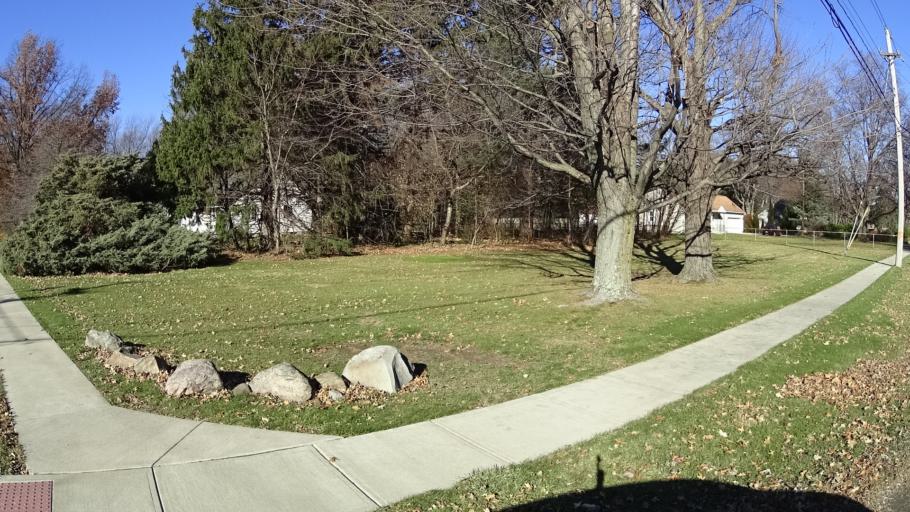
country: US
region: Ohio
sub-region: Lorain County
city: Avon
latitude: 41.4306
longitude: -82.0378
